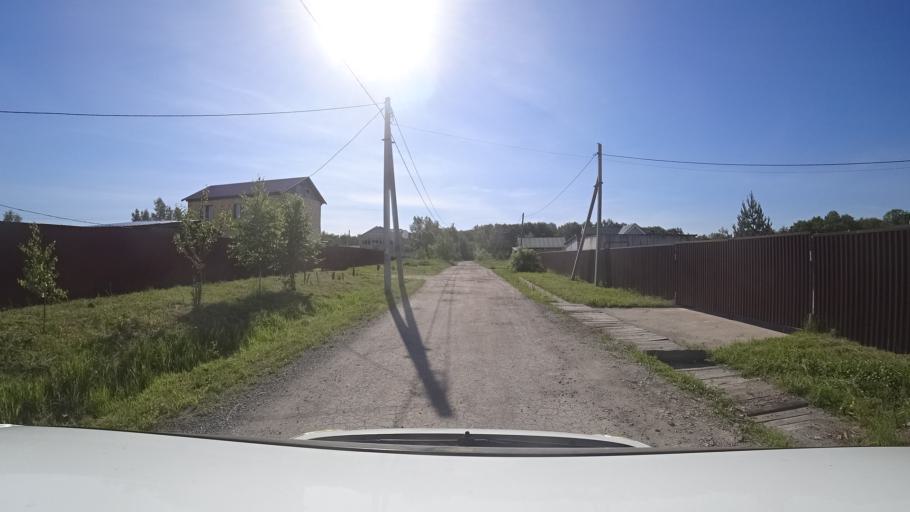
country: RU
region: Khabarovsk Krai
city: Topolevo
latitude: 48.5493
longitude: 135.1823
